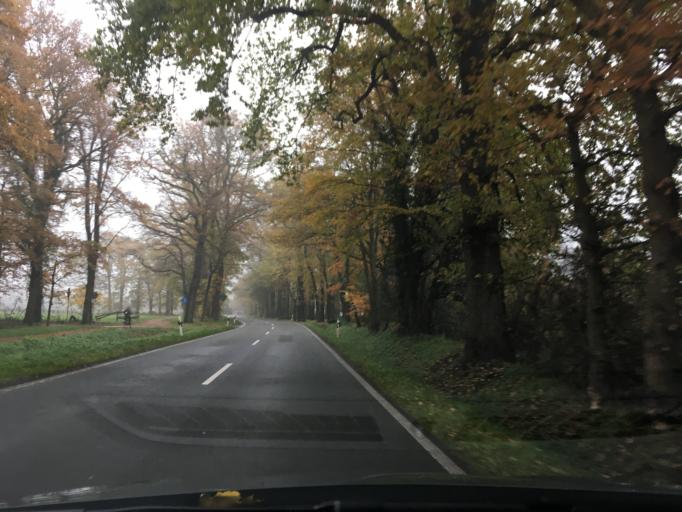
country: DE
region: North Rhine-Westphalia
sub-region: Regierungsbezirk Munster
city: Ahaus
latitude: 52.0782
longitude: 6.9352
